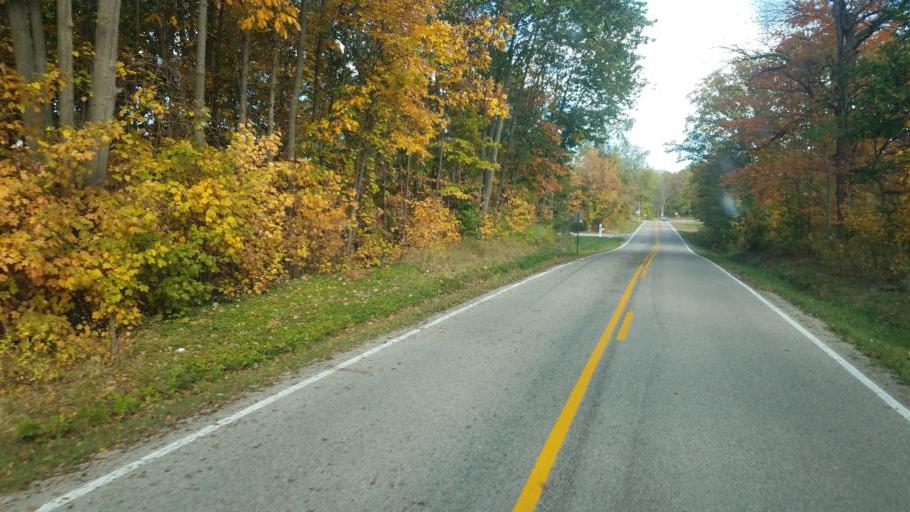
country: US
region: Ohio
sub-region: Huron County
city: New London
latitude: 41.1636
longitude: -82.4520
